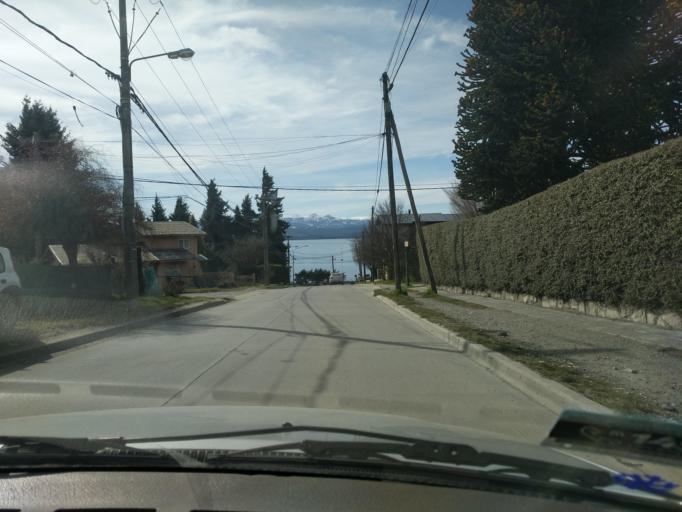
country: AR
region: Rio Negro
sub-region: Departamento de Bariloche
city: San Carlos de Bariloche
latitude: -41.1276
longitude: -71.3547
